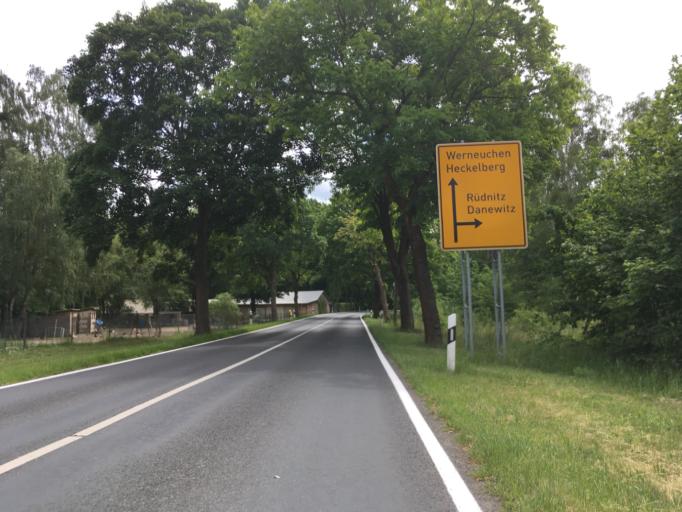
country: DE
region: Brandenburg
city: Melchow
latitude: 52.7510
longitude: 13.6838
